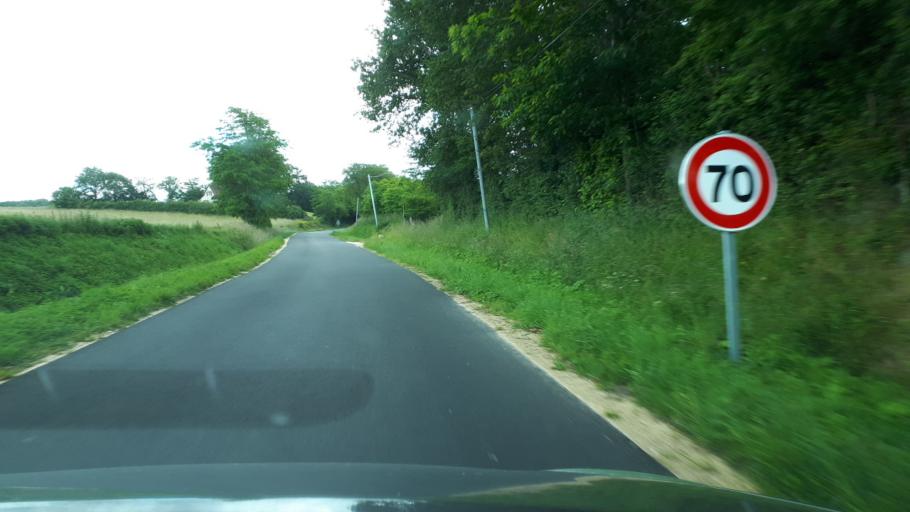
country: FR
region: Centre
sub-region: Departement du Loir-et-Cher
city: Sarge-sur-Braye
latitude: 47.9252
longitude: 0.8642
